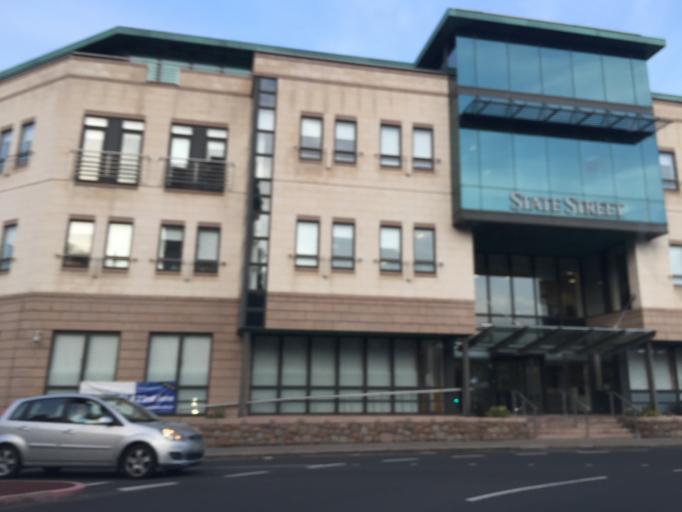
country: JE
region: St Helier
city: Saint Helier
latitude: 49.1805
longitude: -2.1033
